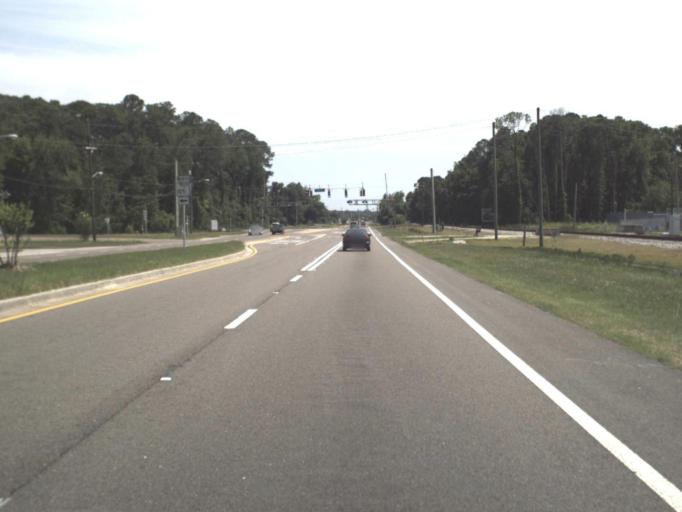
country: US
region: Florida
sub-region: Duval County
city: Jacksonville
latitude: 30.4062
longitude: -81.6500
